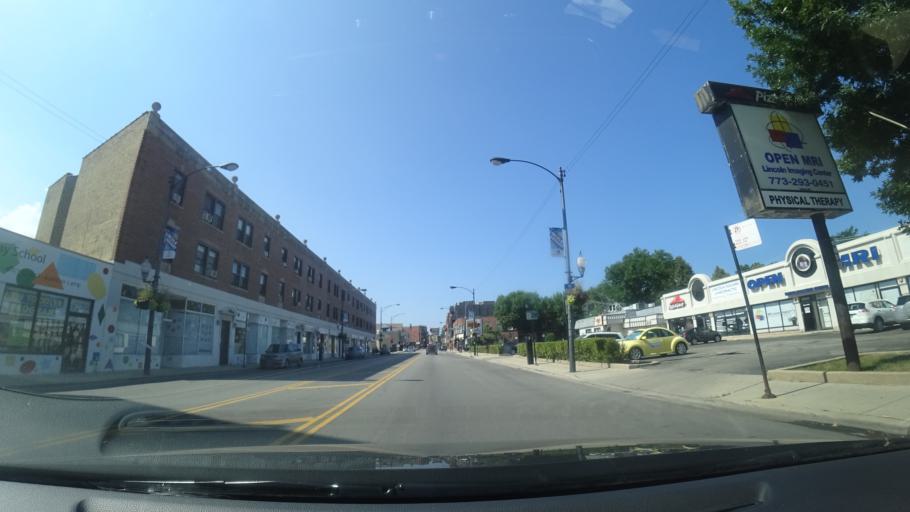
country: US
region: Illinois
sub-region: Cook County
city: Lincolnwood
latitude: 41.9721
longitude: -87.6907
